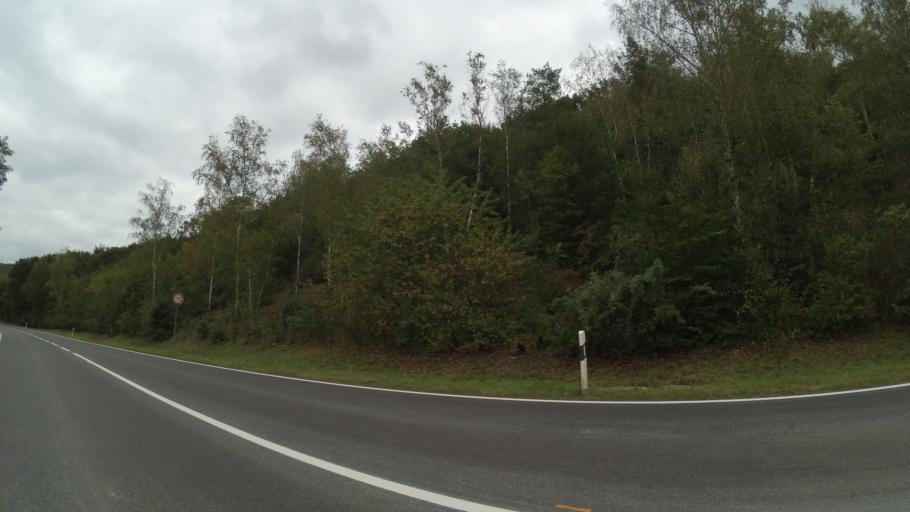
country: DE
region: Saarland
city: Quierschied
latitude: 49.3183
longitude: 7.0551
